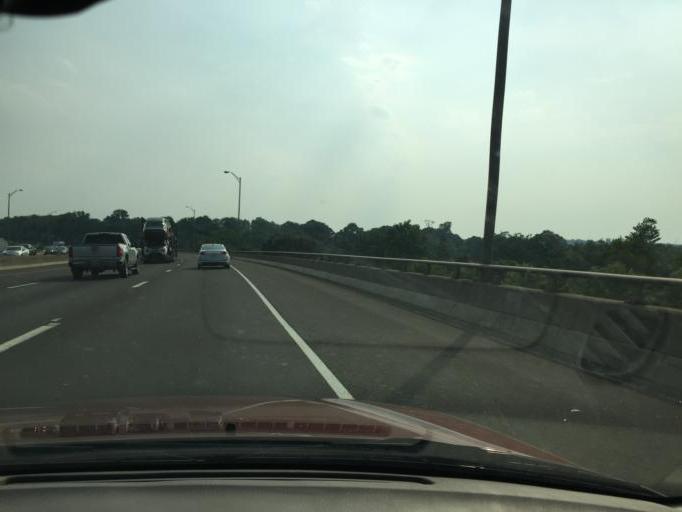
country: US
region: Connecticut
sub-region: Fairfield County
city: Cos Cob
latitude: 41.0359
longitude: -73.5941
